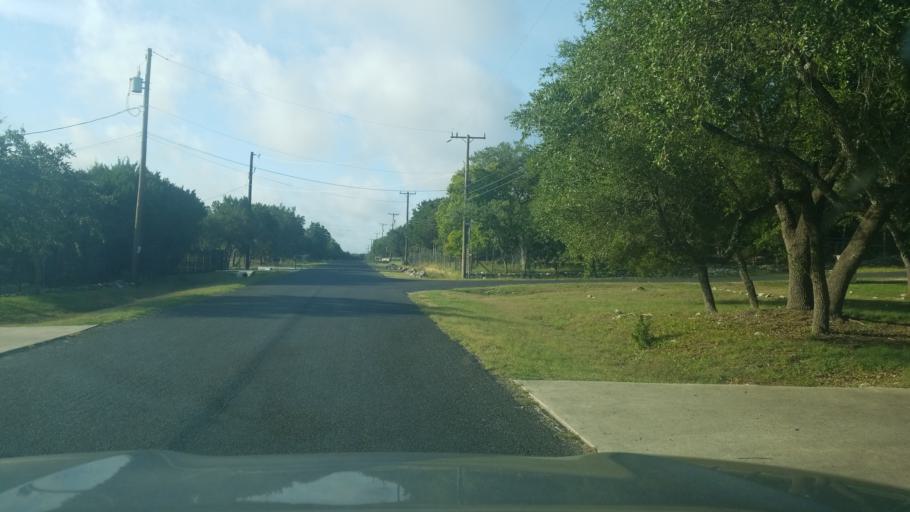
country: US
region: Texas
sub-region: Bexar County
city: Timberwood Park
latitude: 29.7027
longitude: -98.5127
